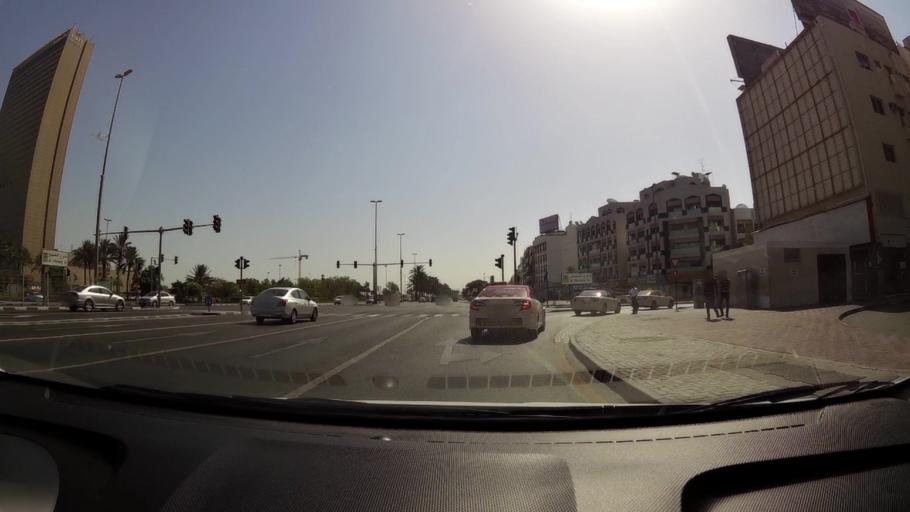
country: AE
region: Ash Shariqah
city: Sharjah
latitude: 25.2765
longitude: 55.3046
